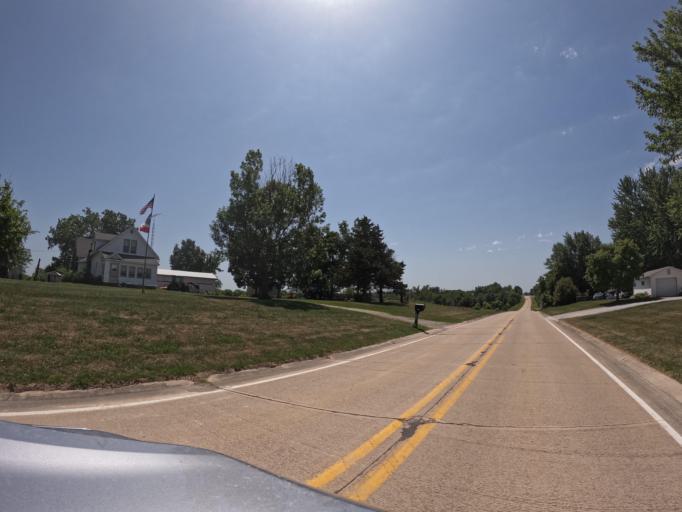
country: US
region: Iowa
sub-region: Henry County
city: Mount Pleasant
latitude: 40.9517
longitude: -91.5545
